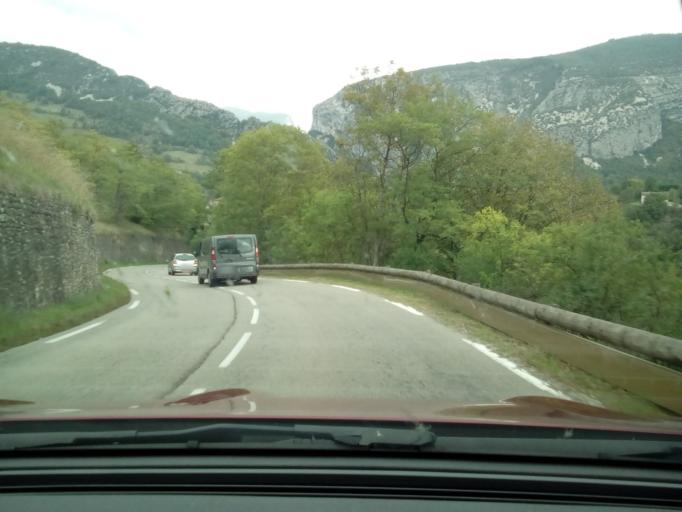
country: FR
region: Rhone-Alpes
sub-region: Departement de l'Isere
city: Pont-en-Royans
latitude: 45.0613
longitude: 5.3297
